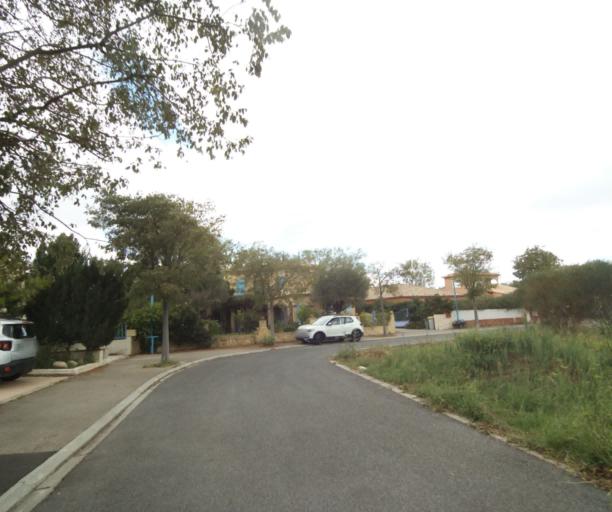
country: FR
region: Languedoc-Roussillon
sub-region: Departement des Pyrenees-Orientales
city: Argelers
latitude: 42.5438
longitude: 3.0464
